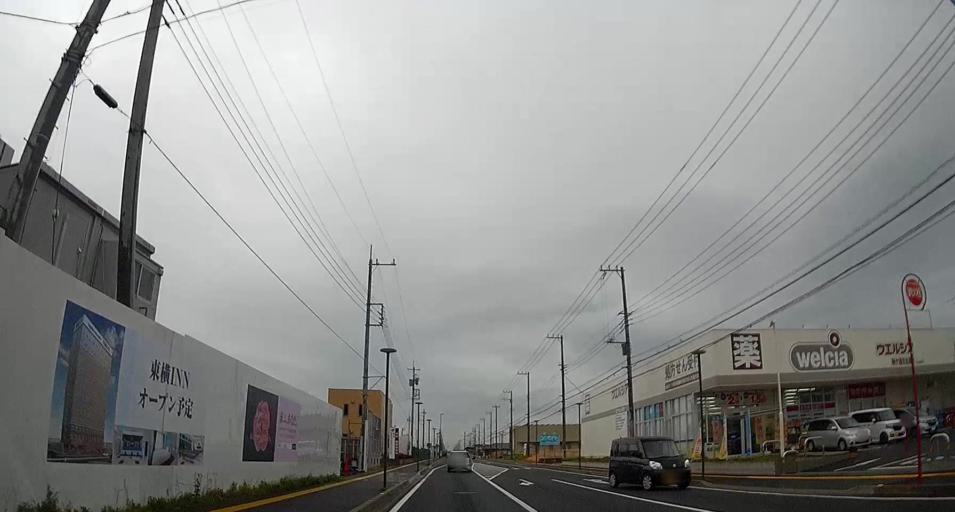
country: JP
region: Chiba
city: Kisarazu
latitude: 35.4338
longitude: 139.9570
